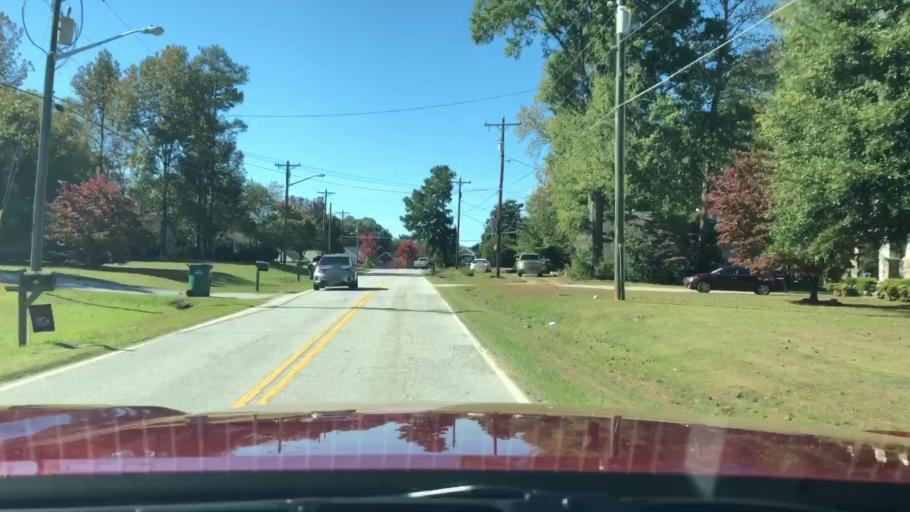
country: US
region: South Carolina
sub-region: Greenwood County
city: Greenwood
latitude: 34.2184
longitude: -82.1372
